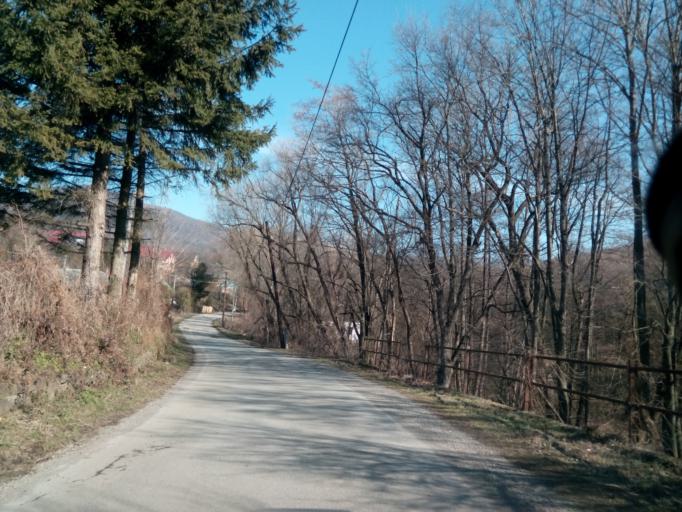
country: SK
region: Kosicky
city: Sobrance
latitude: 48.8515
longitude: 22.1853
